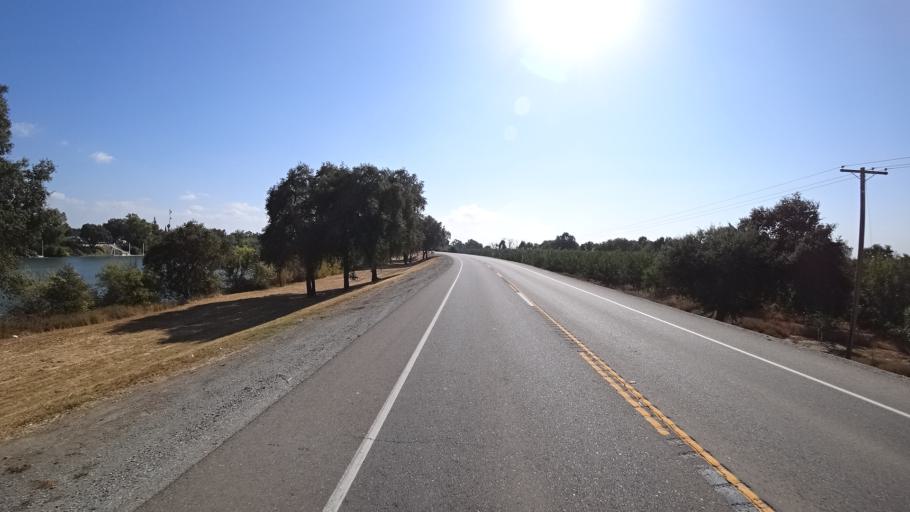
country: US
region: California
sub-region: Yolo County
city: West Sacramento
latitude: 38.6126
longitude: -121.5624
